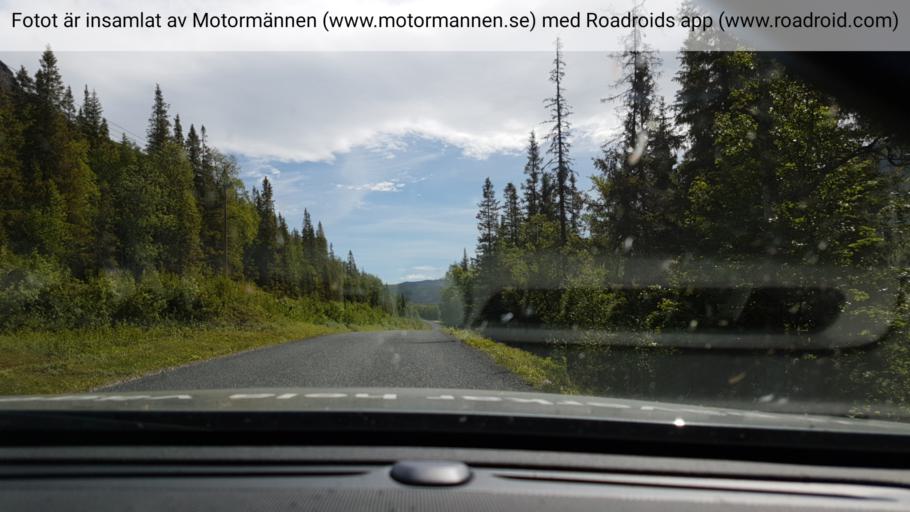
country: SE
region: Vaesterbotten
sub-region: Vilhelmina Kommun
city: Sjoberg
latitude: 65.2428
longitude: 15.4353
